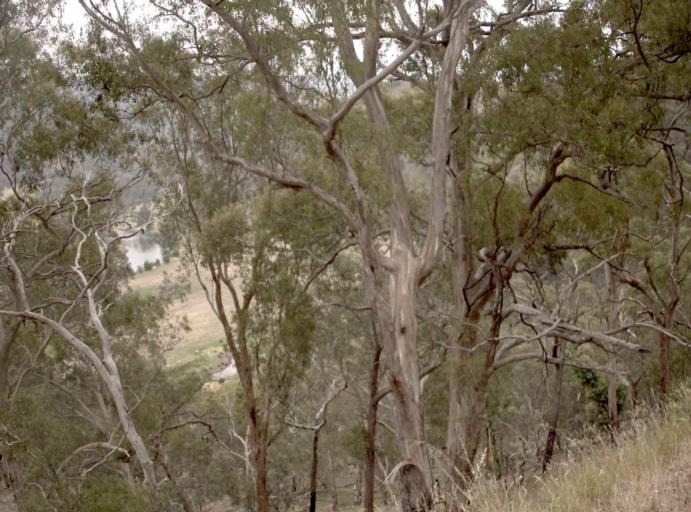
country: AU
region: Victoria
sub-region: Wellington
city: Heyfield
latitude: -37.7055
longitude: 146.6657
